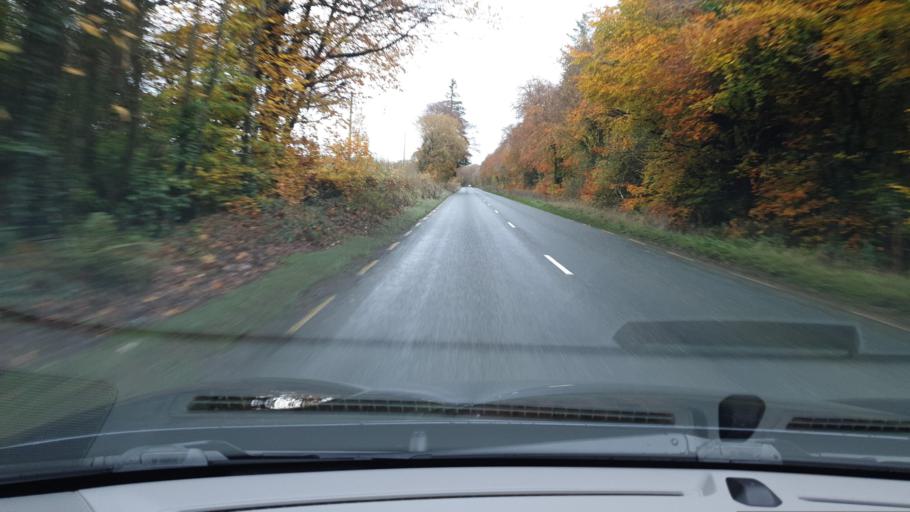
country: IE
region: Leinster
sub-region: Lu
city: Tullyallen
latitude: 53.7983
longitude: -6.4808
